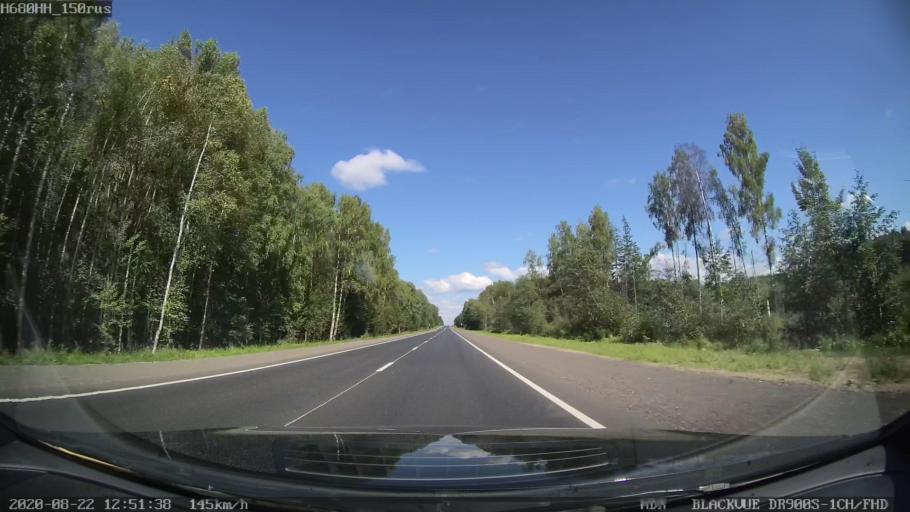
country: RU
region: Tverskaya
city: Rameshki
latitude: 57.4872
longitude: 36.2479
